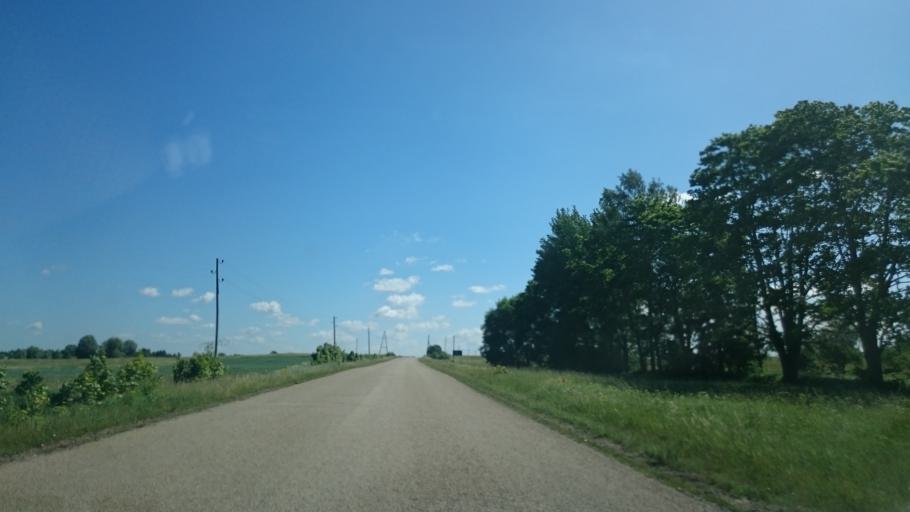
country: LV
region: Cibla
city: Cibla
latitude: 56.5340
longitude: 27.8494
